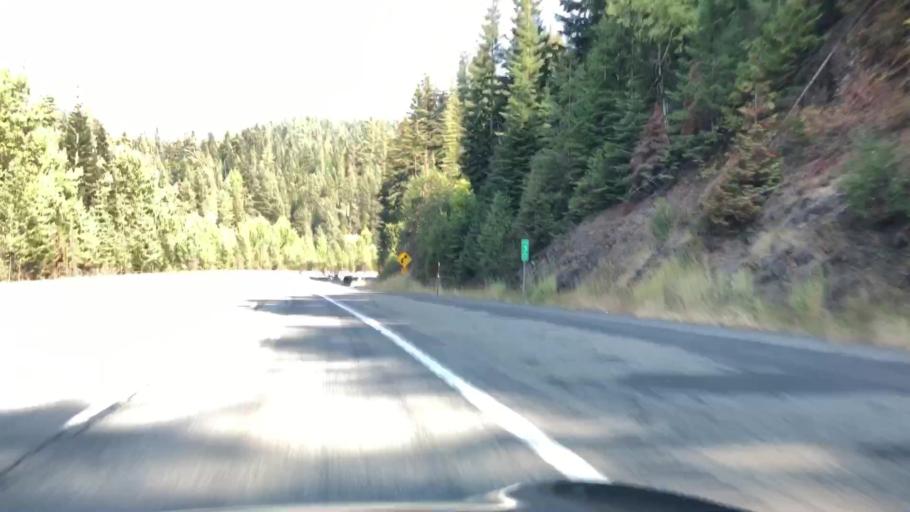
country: US
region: Idaho
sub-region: Shoshone County
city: Pinehurst
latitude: 47.6057
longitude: -116.5067
